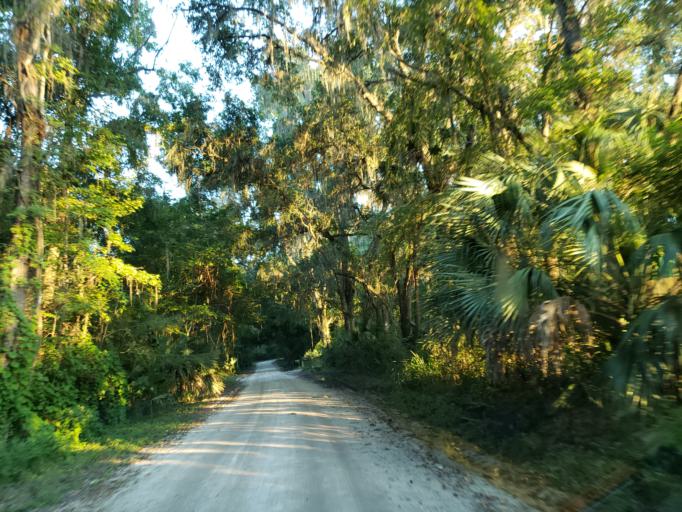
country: US
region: Florida
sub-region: Alachua County
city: Gainesville
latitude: 29.4884
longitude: -82.2783
